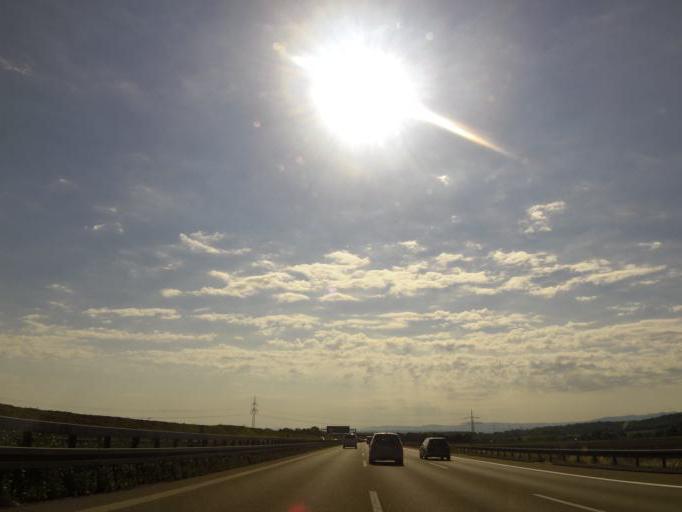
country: DE
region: Baden-Wuerttemberg
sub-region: Regierungsbezirk Stuttgart
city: Neuhausen auf den Fildern
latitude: 48.6940
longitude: 9.2921
